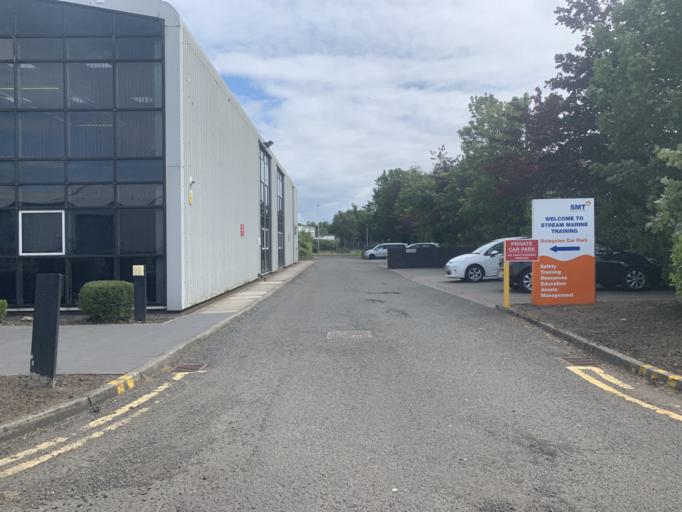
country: GB
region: Scotland
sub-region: Renfrewshire
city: Inchinnan
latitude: 55.8649
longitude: -4.4257
